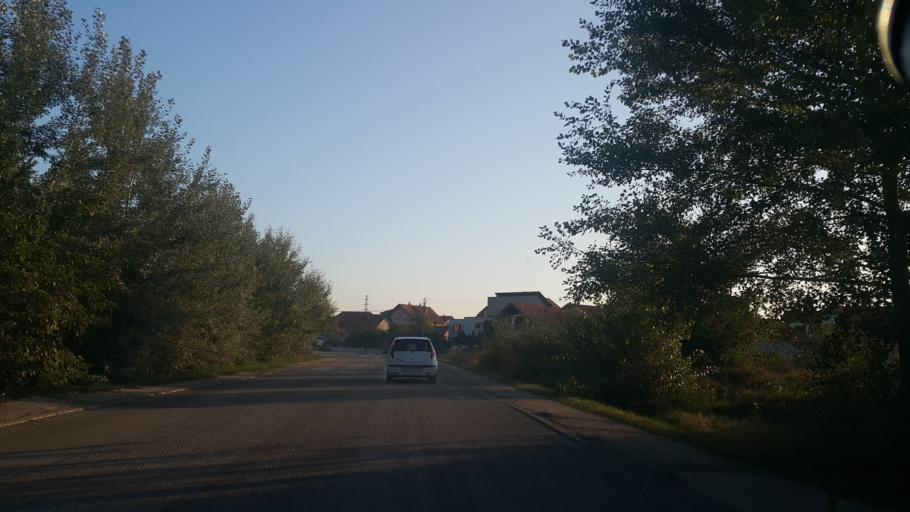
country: RS
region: Central Serbia
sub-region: Zajecarski Okrug
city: Zajecar
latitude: 43.9092
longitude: 22.2962
